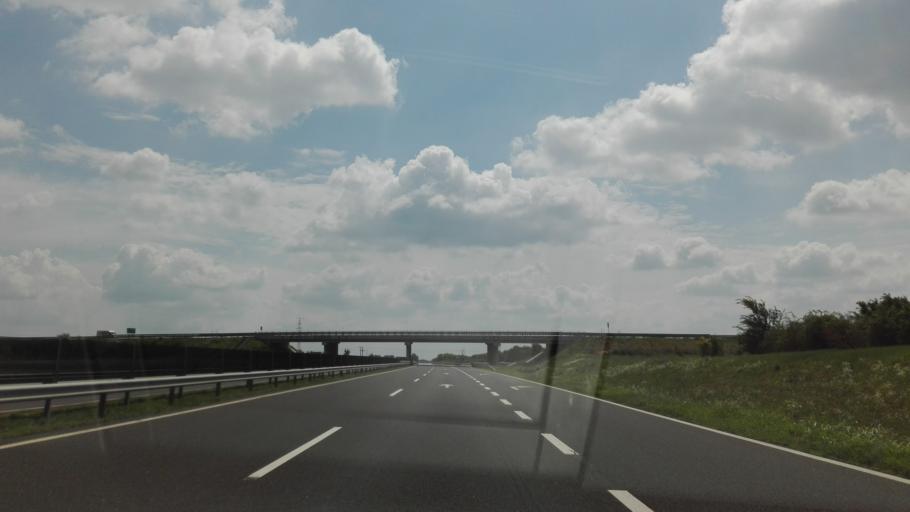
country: HU
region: Fejer
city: dunaujvaros
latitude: 46.9960
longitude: 18.8856
